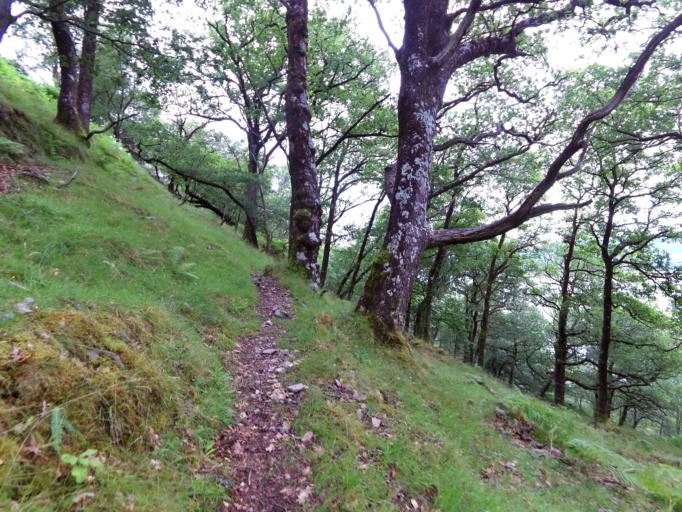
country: GB
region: Scotland
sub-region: Highland
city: Fort William
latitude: 56.8296
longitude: -5.1278
